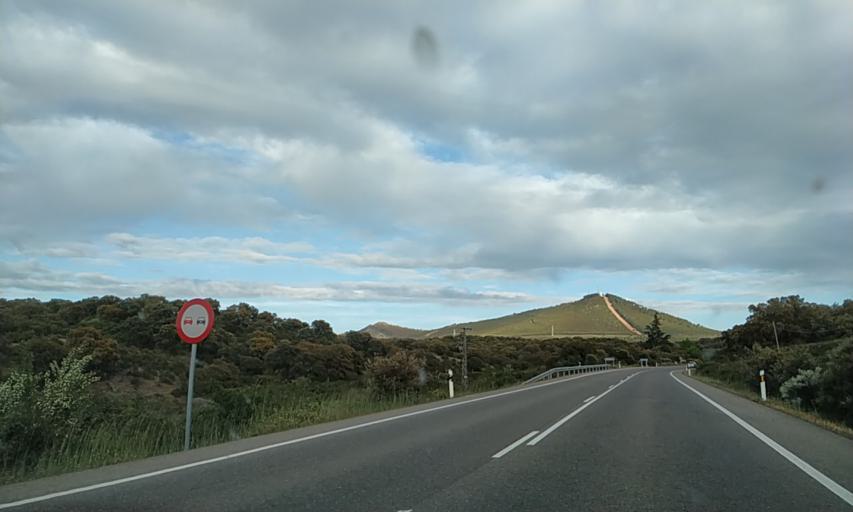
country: ES
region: Extremadura
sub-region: Provincia de Caceres
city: Pedroso de Acim
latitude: 39.8323
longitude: -6.3857
